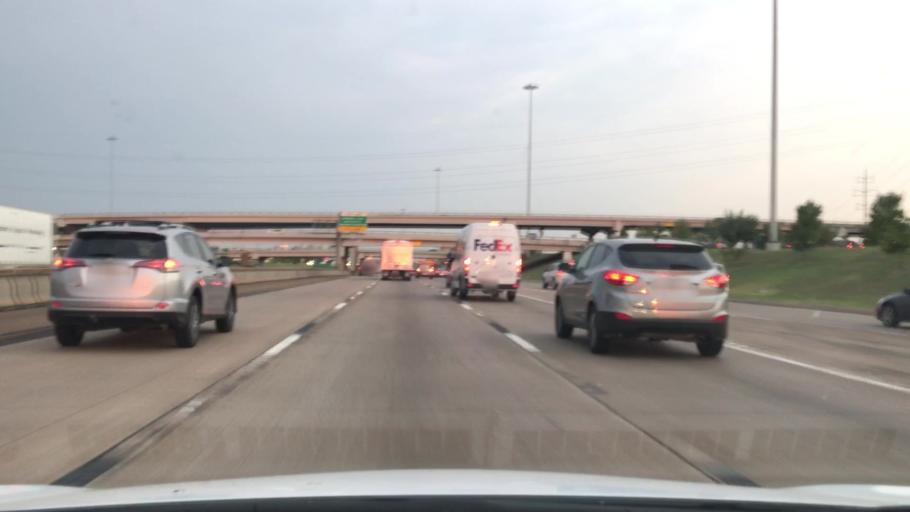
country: US
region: Texas
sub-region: Dallas County
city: Mesquite
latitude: 32.7987
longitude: -96.6803
